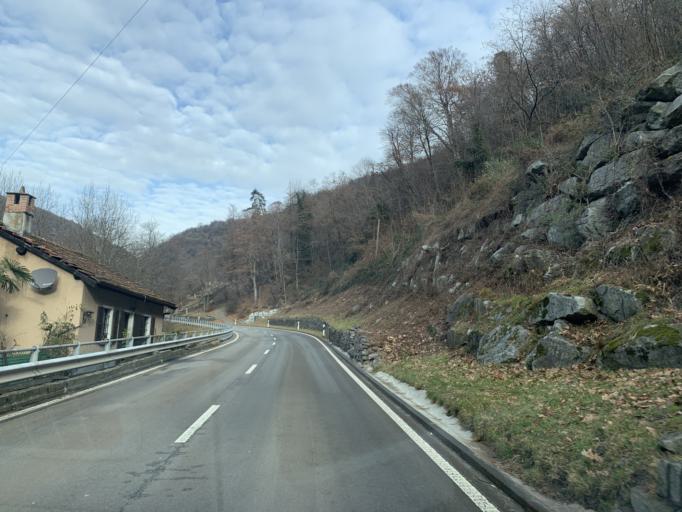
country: CH
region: Ticino
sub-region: Blenio District
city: Cancori
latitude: 46.4160
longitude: 8.8652
